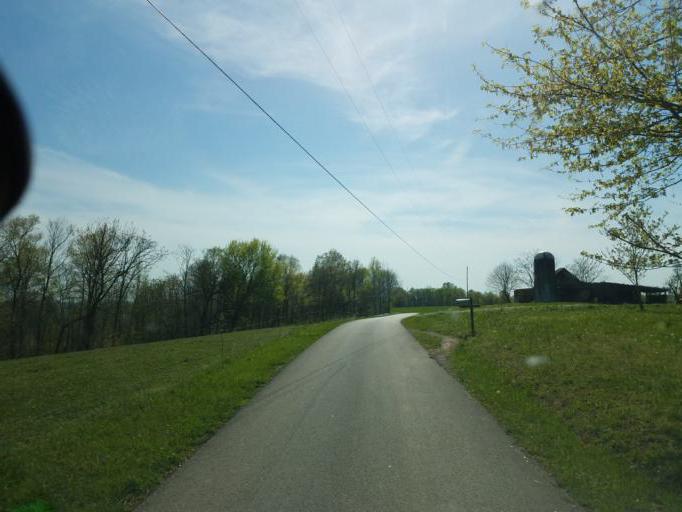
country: US
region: Kentucky
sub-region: Barren County
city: Cave City
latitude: 37.1222
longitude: -86.1021
